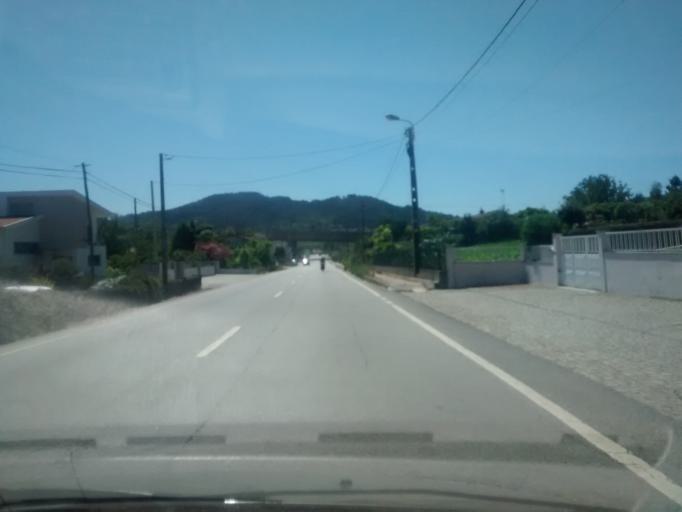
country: PT
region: Braga
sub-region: Braga
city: Oliveira
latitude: 41.5306
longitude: -8.4810
